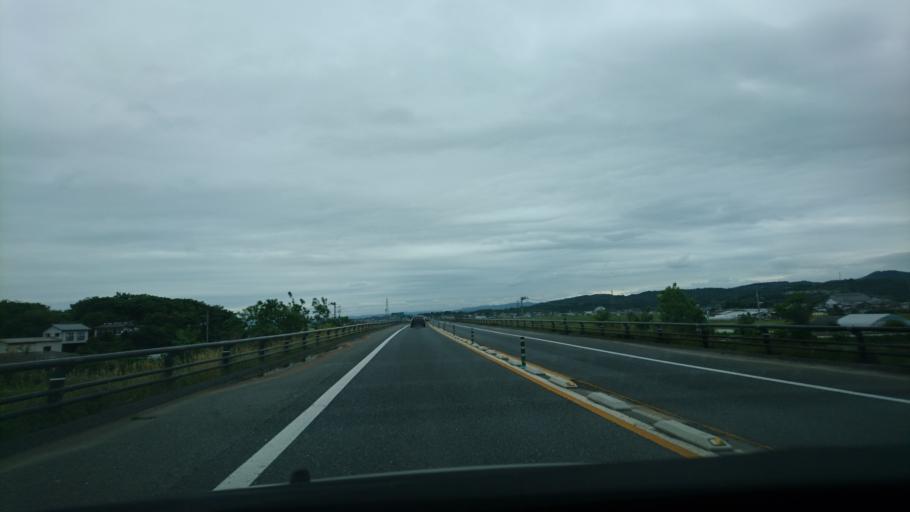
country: JP
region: Miyagi
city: Wakuya
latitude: 38.6479
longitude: 141.2629
